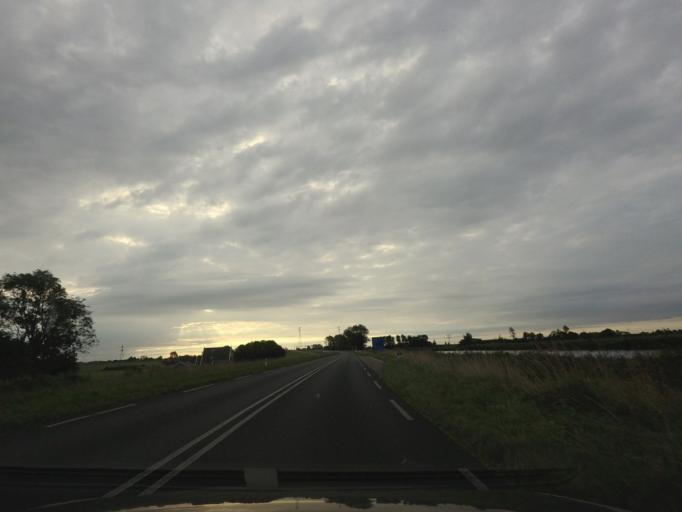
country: NL
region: North Holland
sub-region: Gemeente Uitgeest
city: Uitgeest
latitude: 52.5596
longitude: 4.7750
